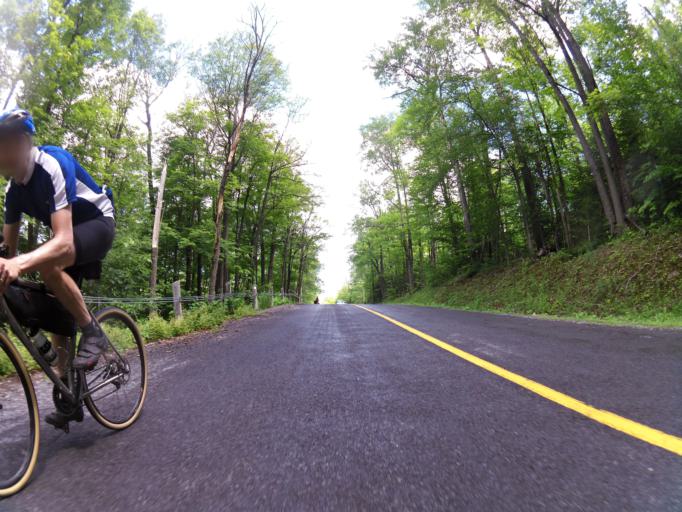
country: CA
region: Ontario
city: Renfrew
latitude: 45.0510
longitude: -76.6737
